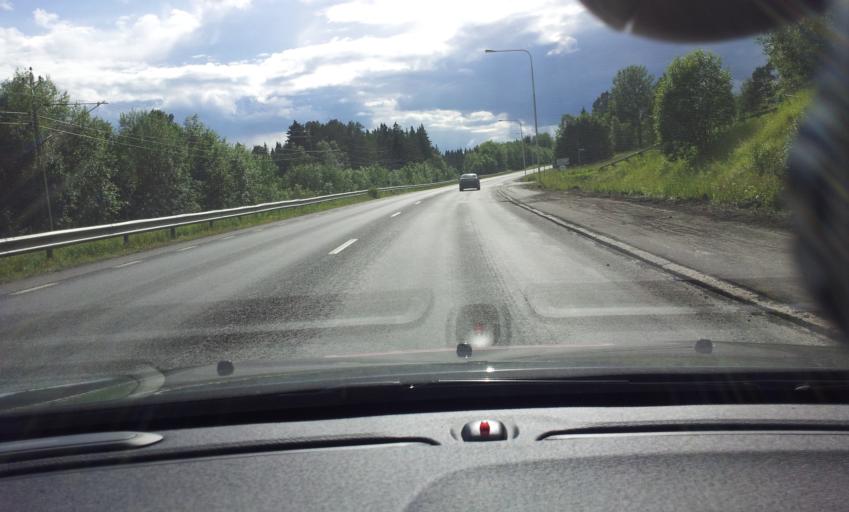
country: SE
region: Jaemtland
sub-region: Are Kommun
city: Jarpen
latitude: 63.3401
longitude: 13.4431
